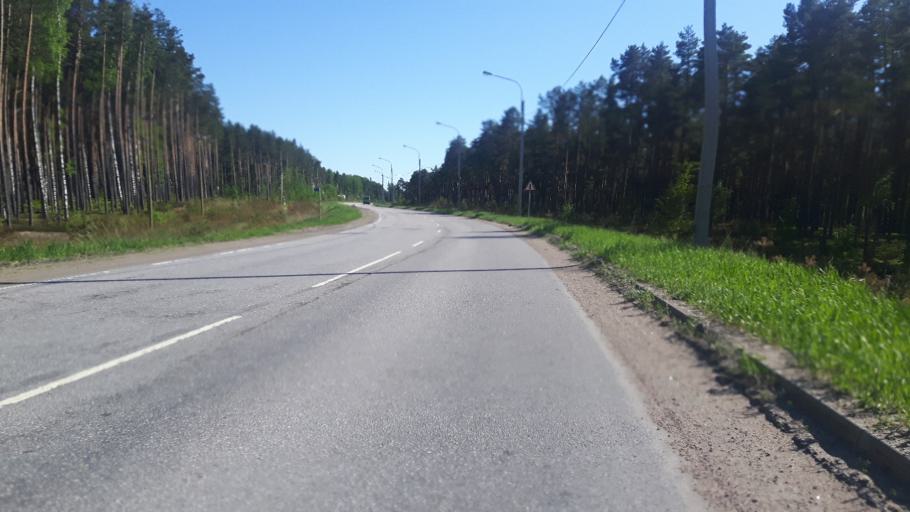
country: RU
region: Leningrad
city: Sosnovyy Bor
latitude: 60.2053
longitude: 29.0052
